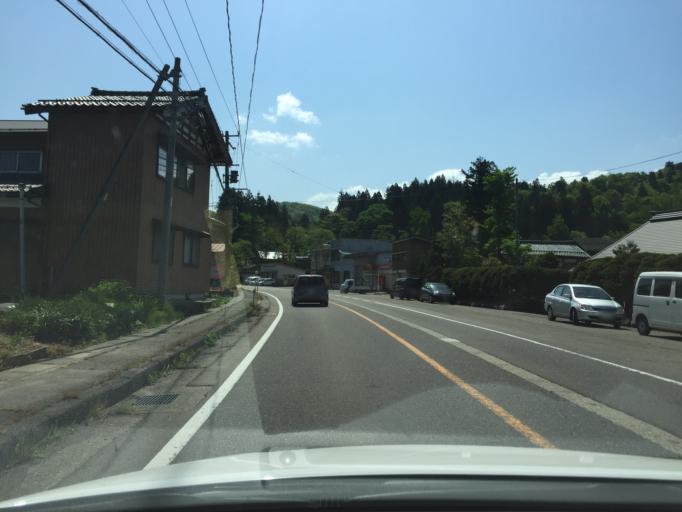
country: JP
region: Niigata
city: Kamo
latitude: 37.6271
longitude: 139.0995
